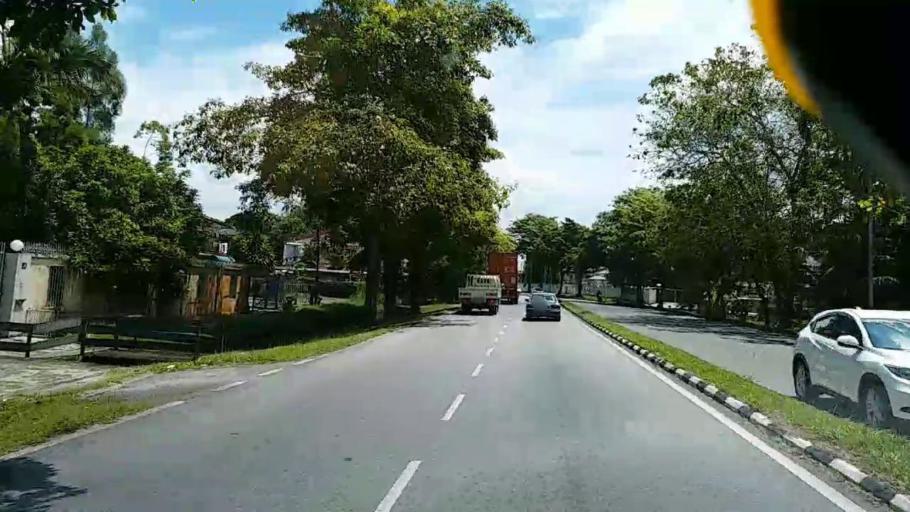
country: MY
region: Sarawak
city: Sibu
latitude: 2.3027
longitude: 111.8347
